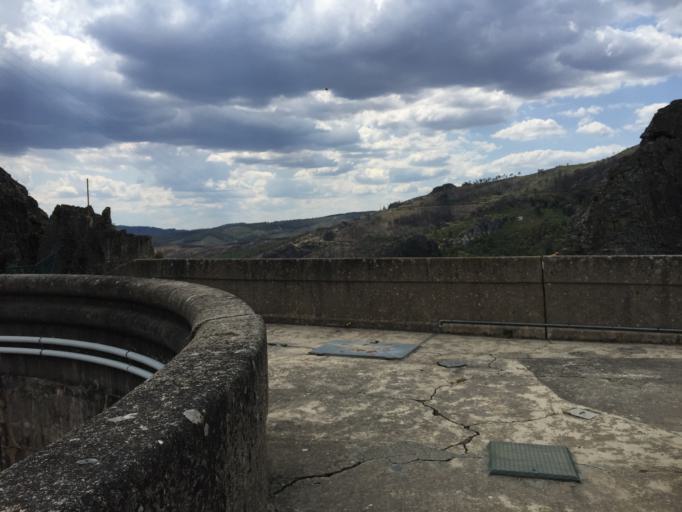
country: PT
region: Coimbra
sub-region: Pampilhosa da Serra
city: Pampilhosa da Serra
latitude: 40.0894
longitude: -7.8579
